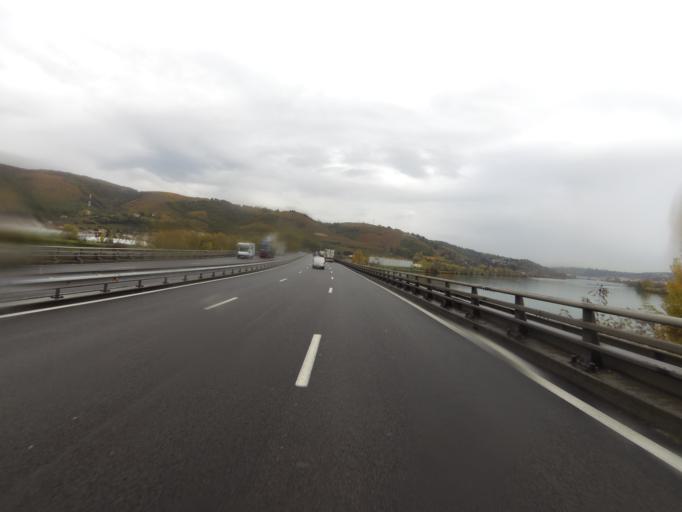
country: FR
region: Rhone-Alpes
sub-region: Departement du Rhone
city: Saint-Cyr-sur-le-Rhone
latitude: 45.4983
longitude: 4.8393
